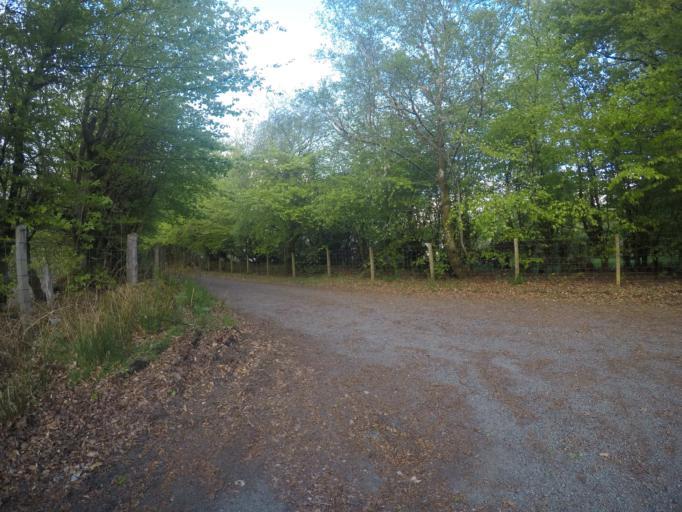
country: GB
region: Scotland
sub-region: Highland
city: Isle of Skye
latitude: 57.4522
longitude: -6.3044
